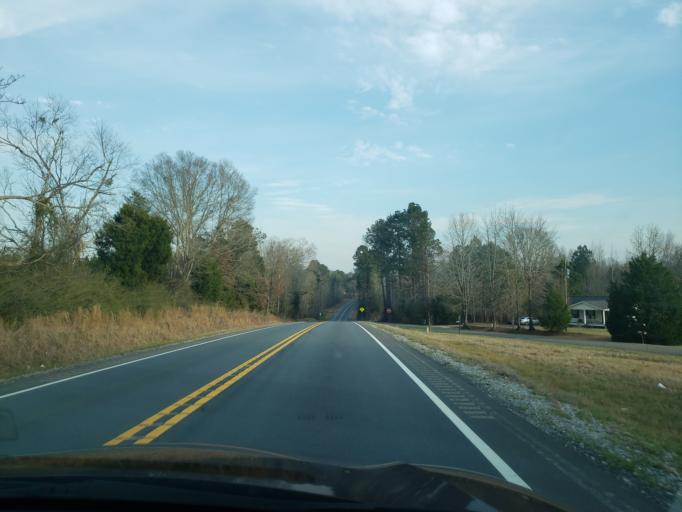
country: US
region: Alabama
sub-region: Hale County
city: Moundville
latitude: 32.8922
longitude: -87.6152
